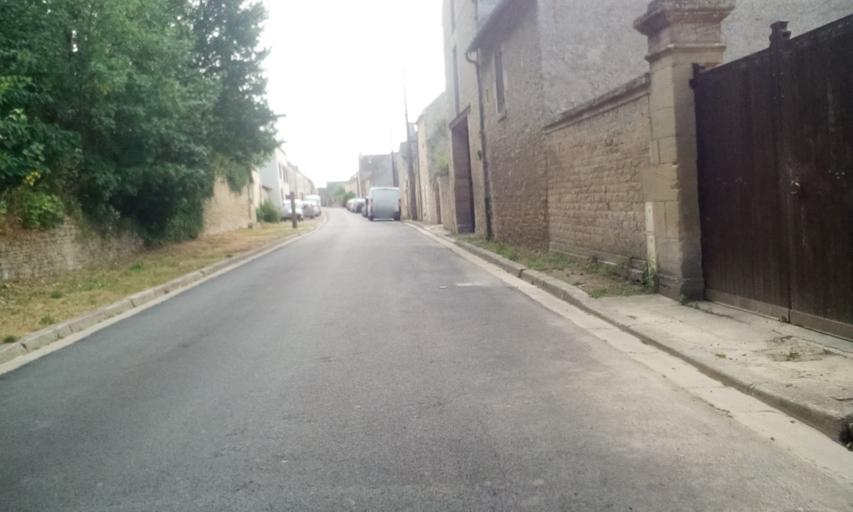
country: FR
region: Lower Normandy
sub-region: Departement du Calvados
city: Courseulles-sur-Mer
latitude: 49.3100
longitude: -0.4911
